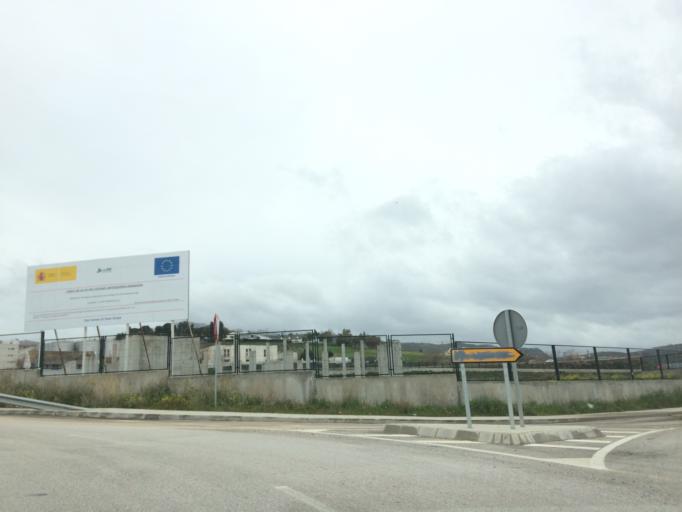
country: ES
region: Andalusia
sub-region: Provincia de Malaga
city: Antequera
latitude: 37.0303
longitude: -4.5609
